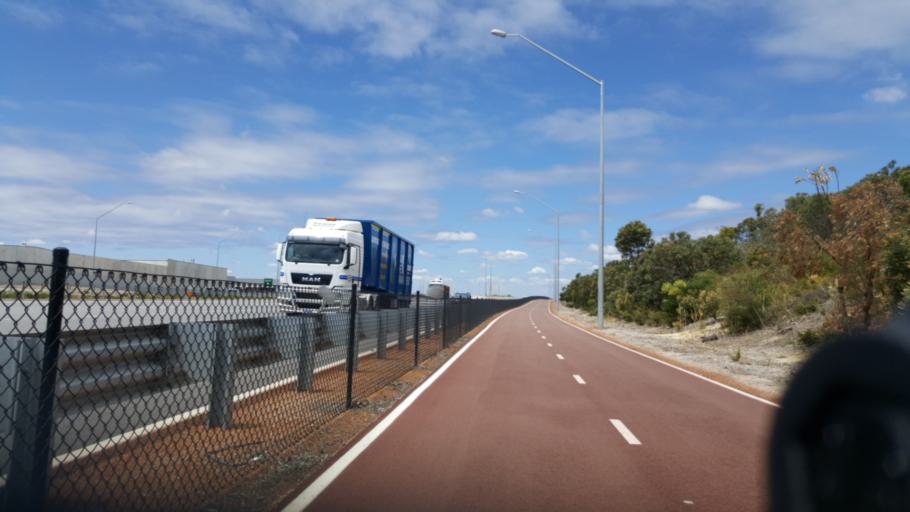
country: AU
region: Western Australia
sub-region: Bayswater
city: Embleton
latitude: -31.8663
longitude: 115.9083
